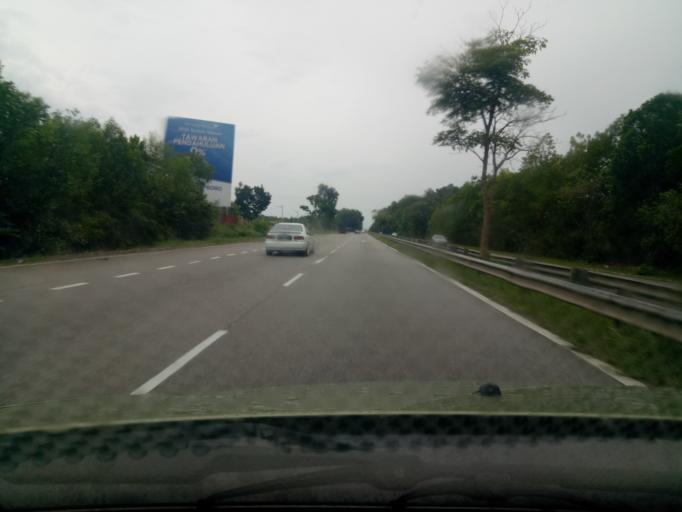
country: MY
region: Kedah
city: Sungai Petani
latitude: 5.6680
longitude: 100.5187
